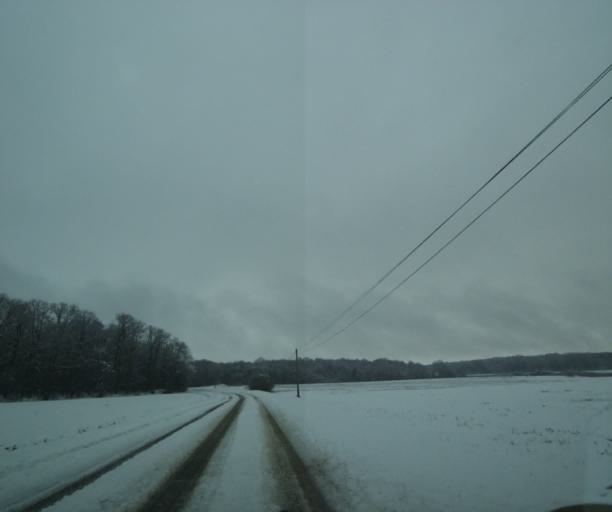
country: FR
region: Champagne-Ardenne
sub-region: Departement de la Haute-Marne
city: Montier-en-Der
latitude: 48.5461
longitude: 4.7997
